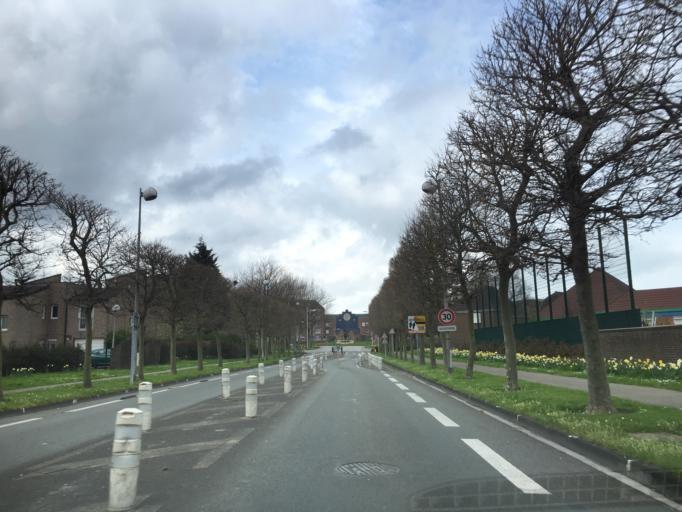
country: FR
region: Nord-Pas-de-Calais
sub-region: Departement du Nord
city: Grande-Synthe
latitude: 51.0080
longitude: 2.3091
